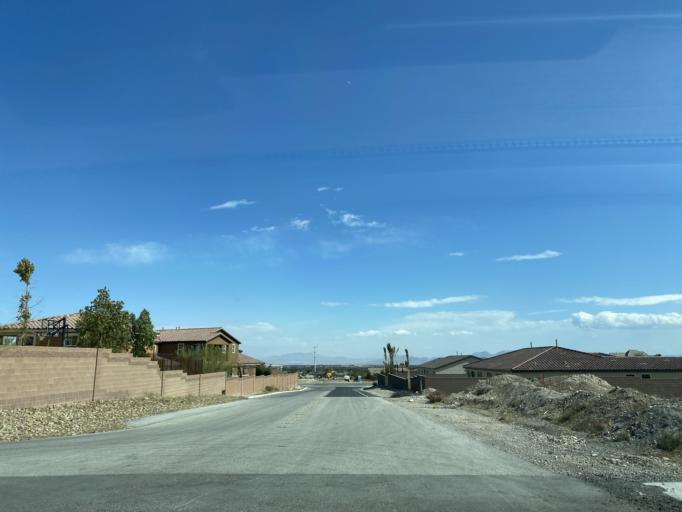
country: US
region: Nevada
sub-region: Clark County
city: Summerlin South
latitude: 36.2499
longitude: -115.3078
